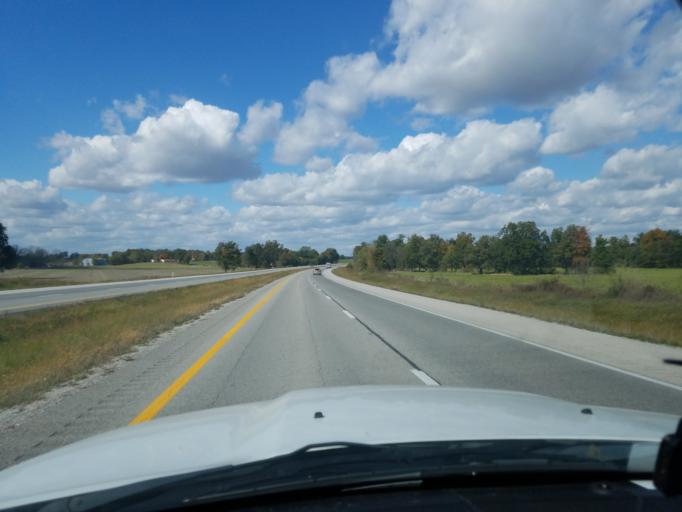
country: US
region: Kentucky
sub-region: Daviess County
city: Masonville
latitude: 37.6651
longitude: -87.0188
